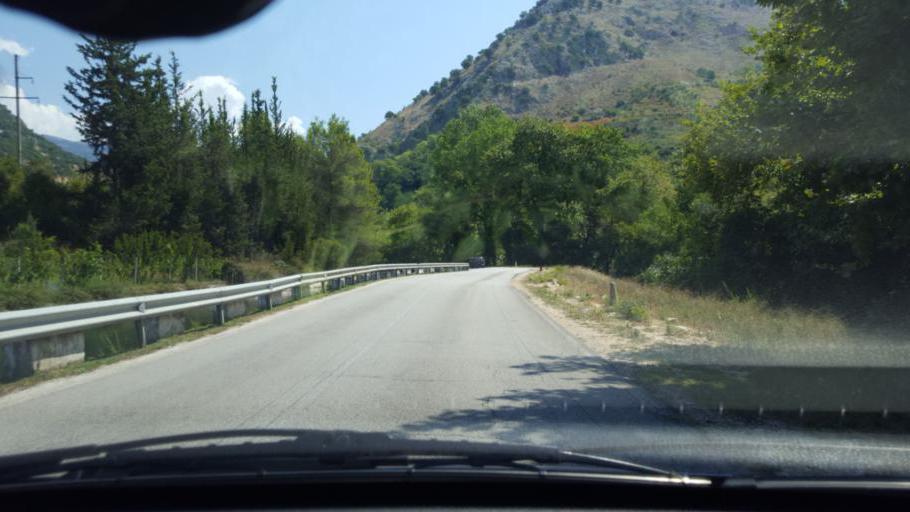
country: AL
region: Vlore
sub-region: Rrethi i Delvines
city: Mesopotam
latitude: 39.9159
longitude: 20.1333
